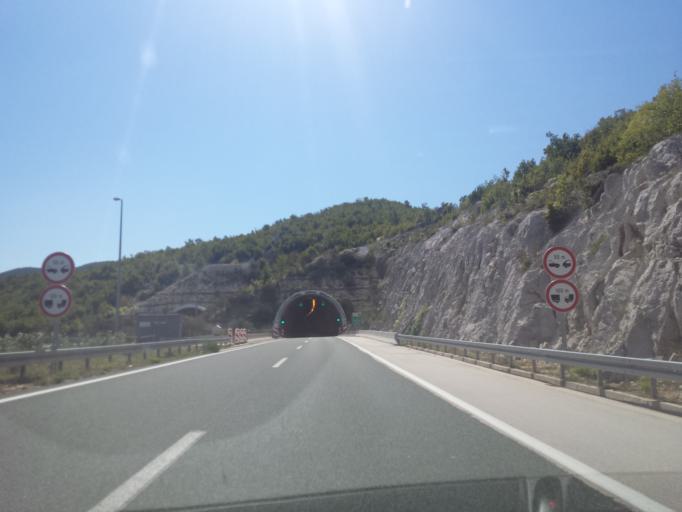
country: HR
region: Splitsko-Dalmatinska
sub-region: Grad Omis
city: Omis
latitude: 43.4870
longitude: 16.8002
